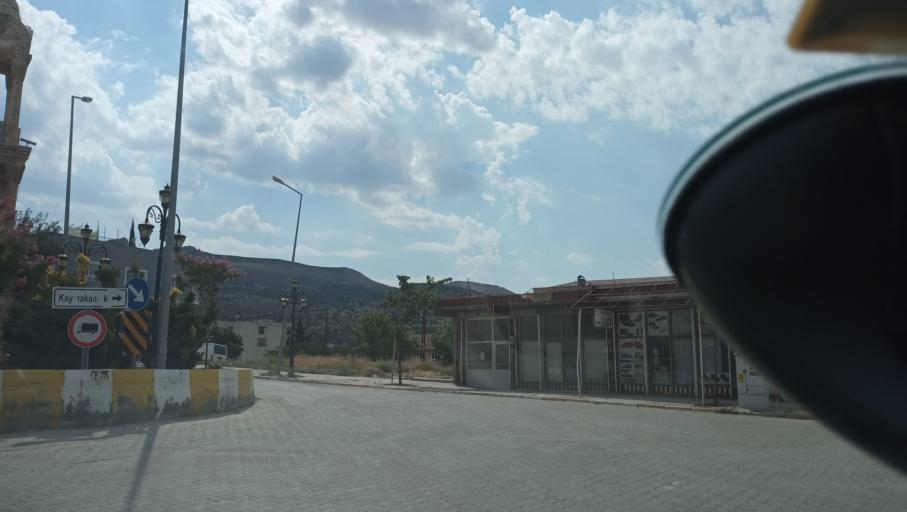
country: TR
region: Mardin
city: Yesilli
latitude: 37.3391
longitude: 40.8200
